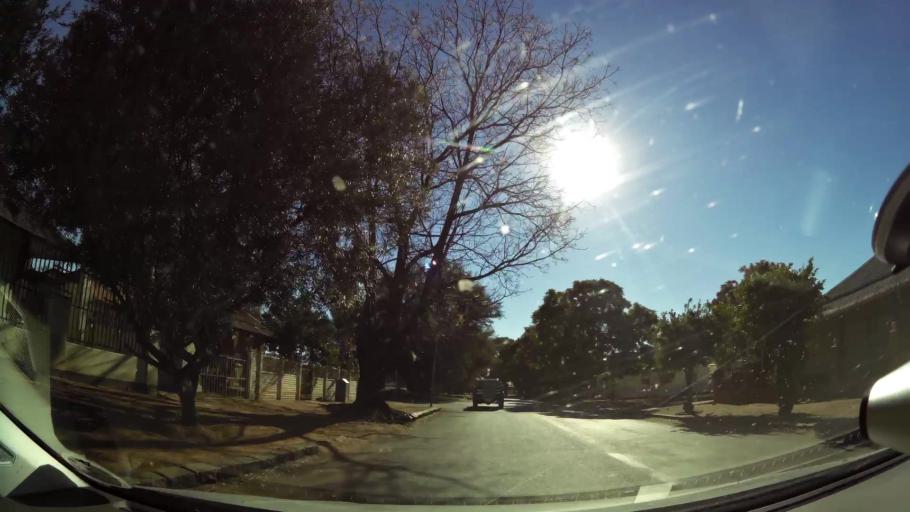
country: ZA
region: Northern Cape
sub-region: Frances Baard District Municipality
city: Kimberley
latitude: -28.7311
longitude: 24.7678
